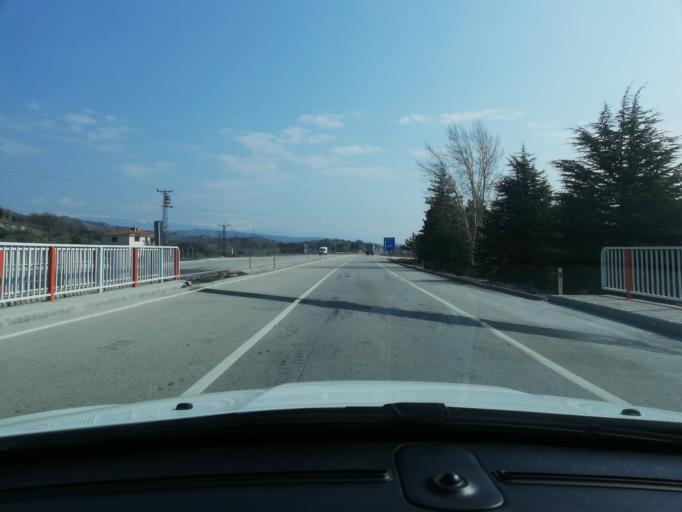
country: TR
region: Cankiri
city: Beloren
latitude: 40.8660
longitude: 33.4856
